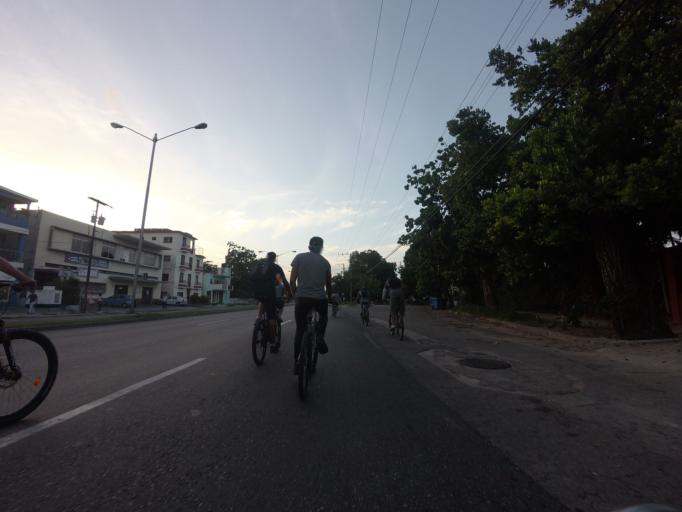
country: CU
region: La Habana
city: Havana
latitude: 23.1187
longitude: -82.4023
